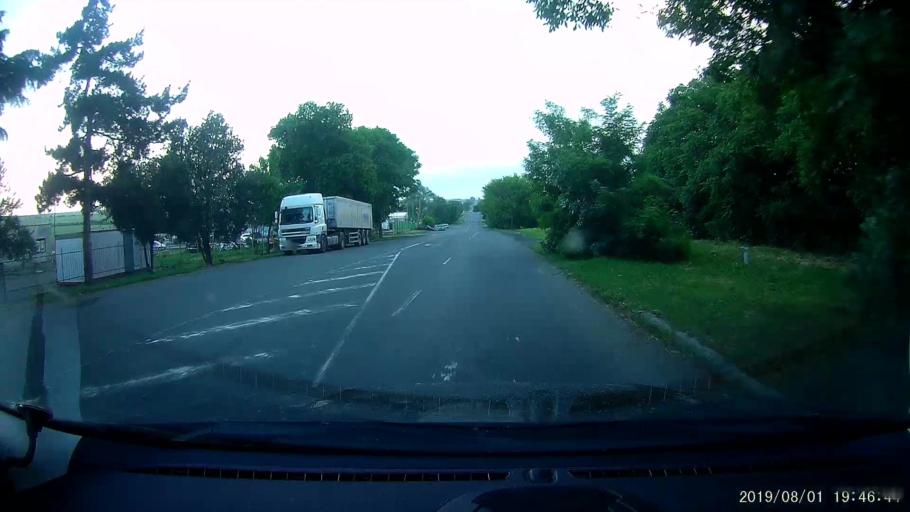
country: BG
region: Burgas
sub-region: Obshtina Karnobat
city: Karnobat
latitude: 42.6499
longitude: 26.9680
